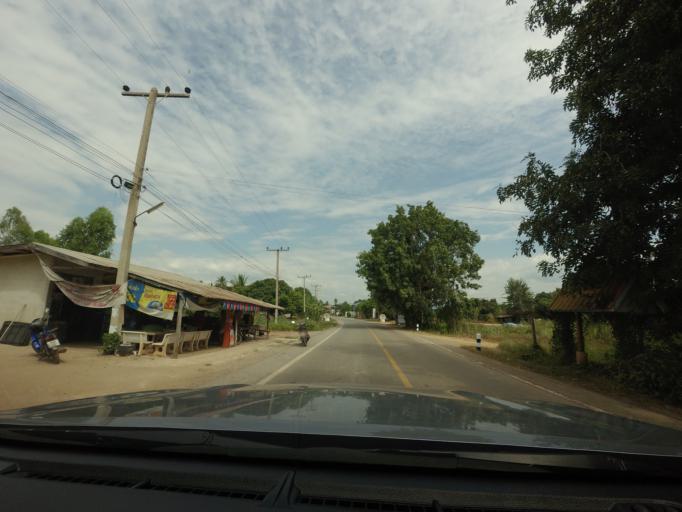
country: TH
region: Phitsanulok
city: Wang Thong
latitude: 16.7290
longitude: 100.3771
